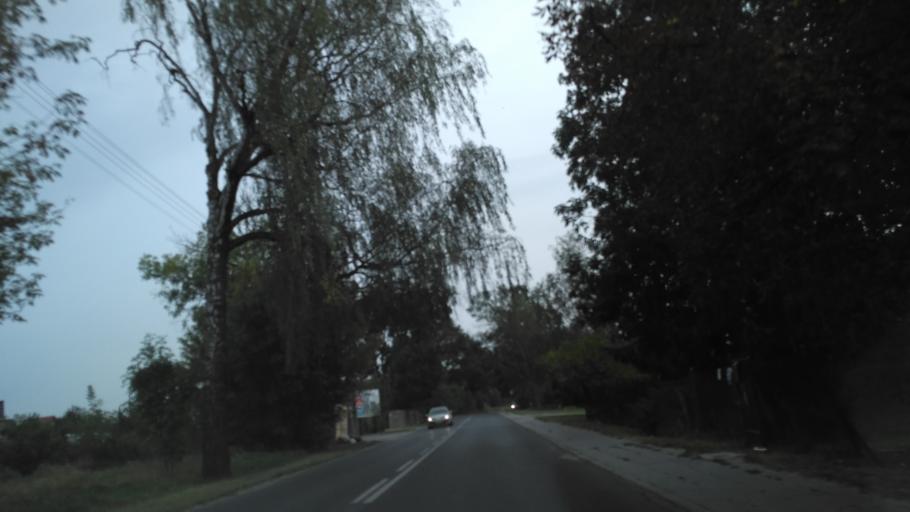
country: PL
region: Lublin Voivodeship
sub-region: Powiat lubelski
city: Lublin
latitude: 51.2098
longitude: 22.5964
